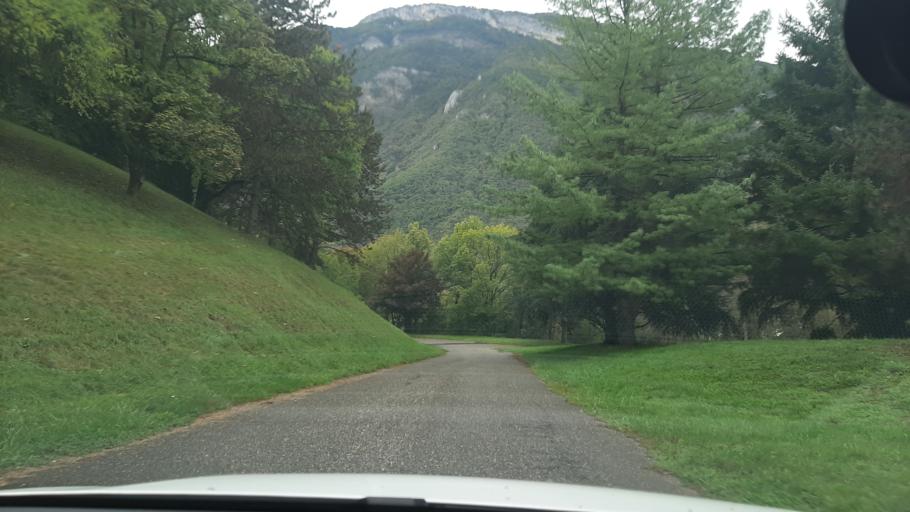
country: FR
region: Rhone-Alpes
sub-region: Departement de la Savoie
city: Montmelian
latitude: 45.5004
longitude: 6.0563
